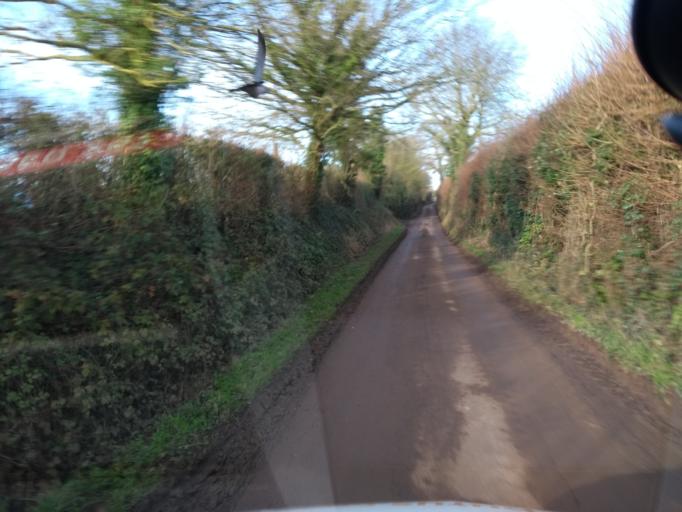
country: GB
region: England
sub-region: Somerset
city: Creech Saint Michael
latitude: 51.0155
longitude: -2.9779
